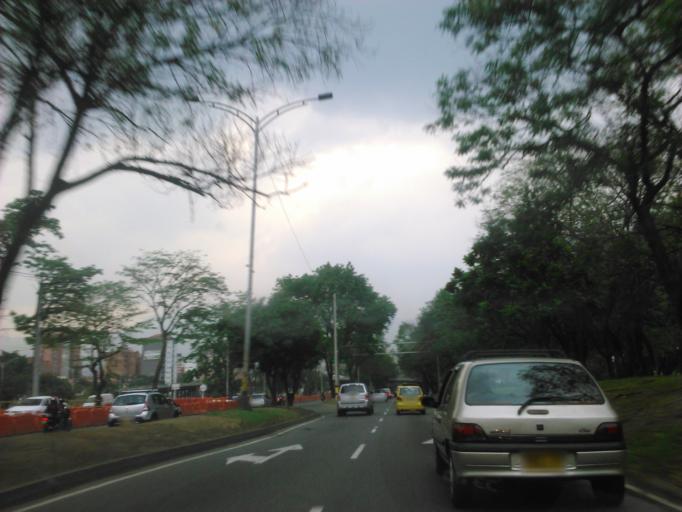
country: CO
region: Antioquia
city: Medellin
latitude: 6.2378
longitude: -75.5763
